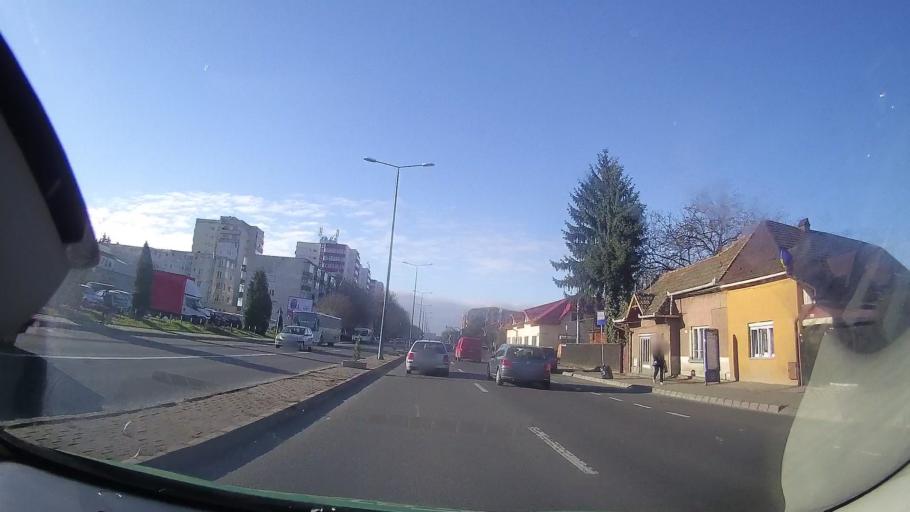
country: RO
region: Mures
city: Targu-Mures
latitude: 46.5246
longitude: 24.5368
